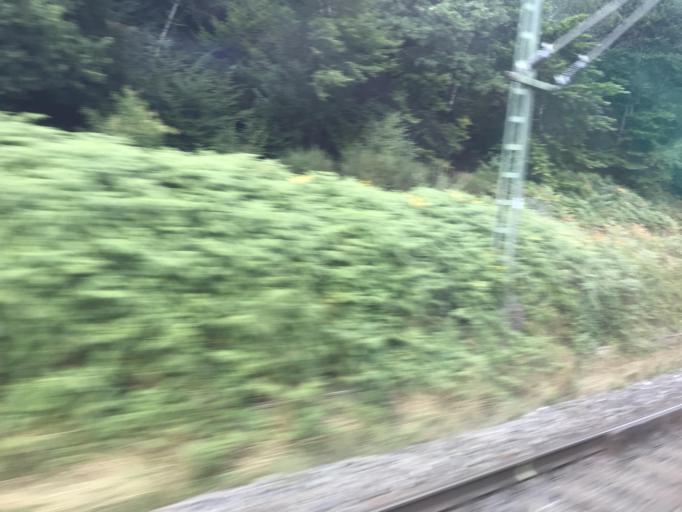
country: DE
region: North Rhine-Westphalia
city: Stolberg
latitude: 50.8013
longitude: 6.2316
